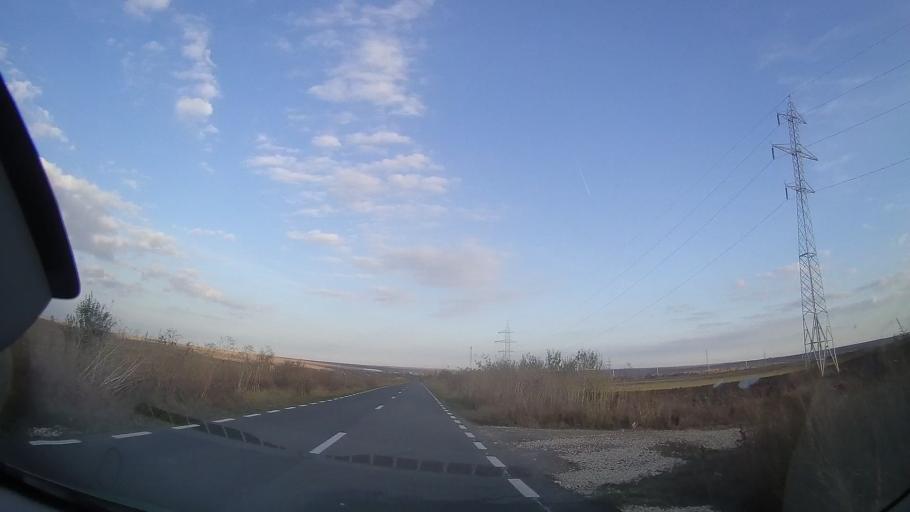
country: RO
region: Constanta
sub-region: Comuna Chirnogeni
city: Plopeni
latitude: 43.9516
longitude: 28.1699
